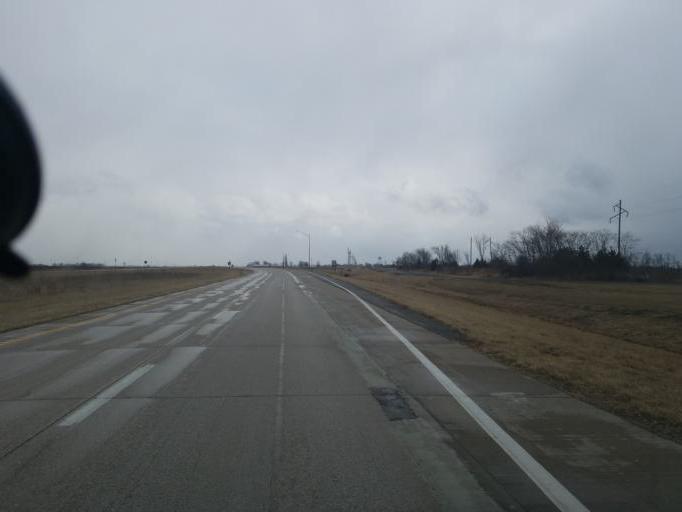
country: US
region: Missouri
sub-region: Randolph County
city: Moberly
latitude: 39.5339
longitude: -92.4465
